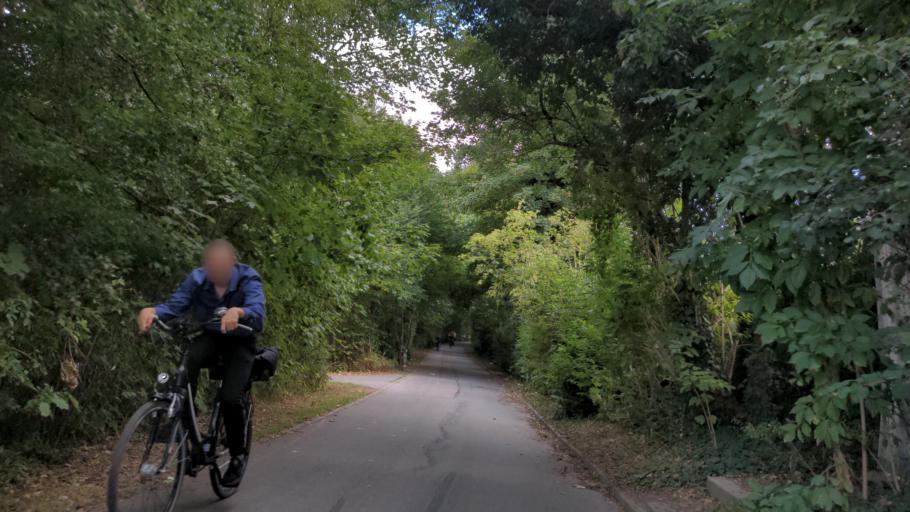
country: DE
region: Mecklenburg-Vorpommern
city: Wismar
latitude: 53.8951
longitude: 11.4355
